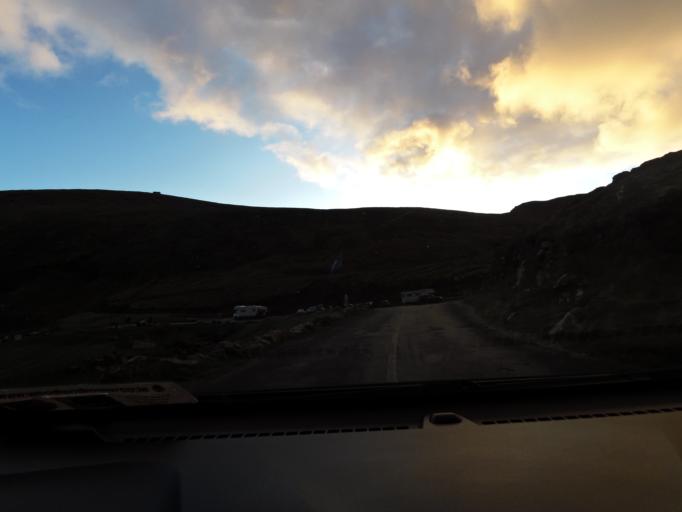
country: IE
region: Connaught
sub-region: Maigh Eo
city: Belmullet
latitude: 53.9678
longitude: -10.1949
